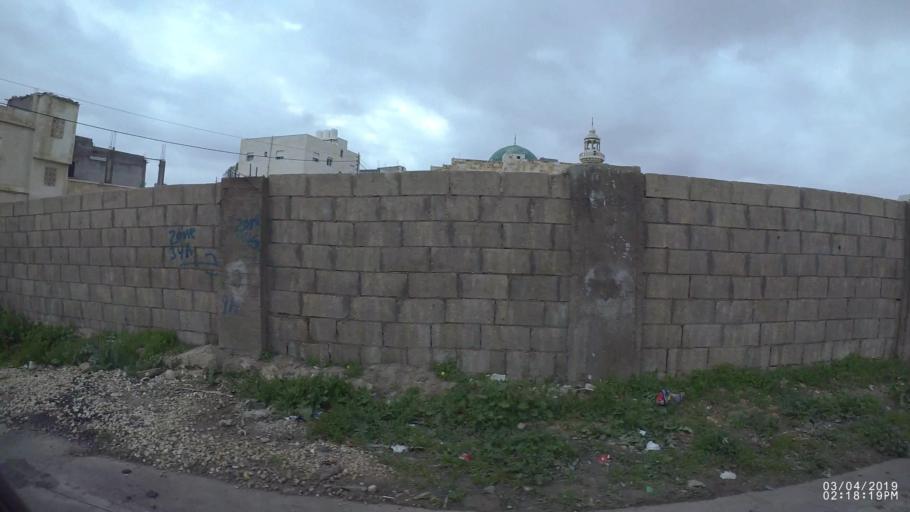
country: JO
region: Amman
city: Wadi as Sir
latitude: 31.9409
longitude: 35.8323
